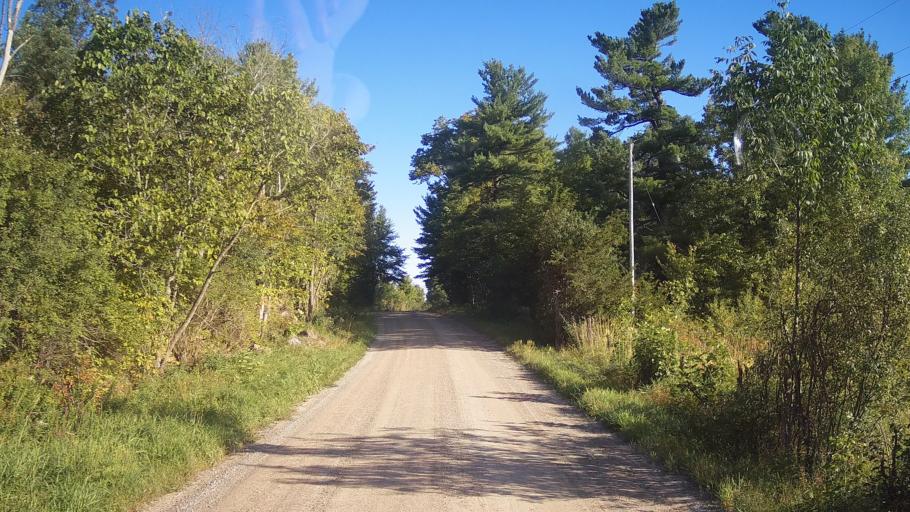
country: US
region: New York
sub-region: Jefferson County
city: Alexandria Bay
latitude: 44.4135
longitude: -75.9768
